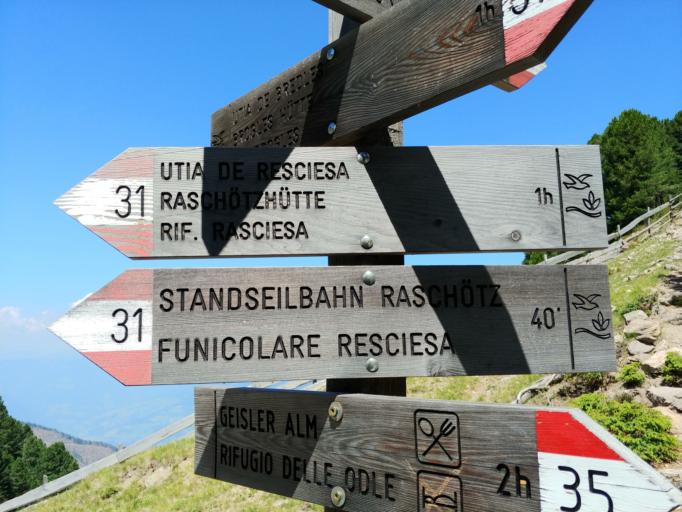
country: IT
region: Trentino-Alto Adige
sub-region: Bolzano
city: San Pietro
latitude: 46.6079
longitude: 11.6837
